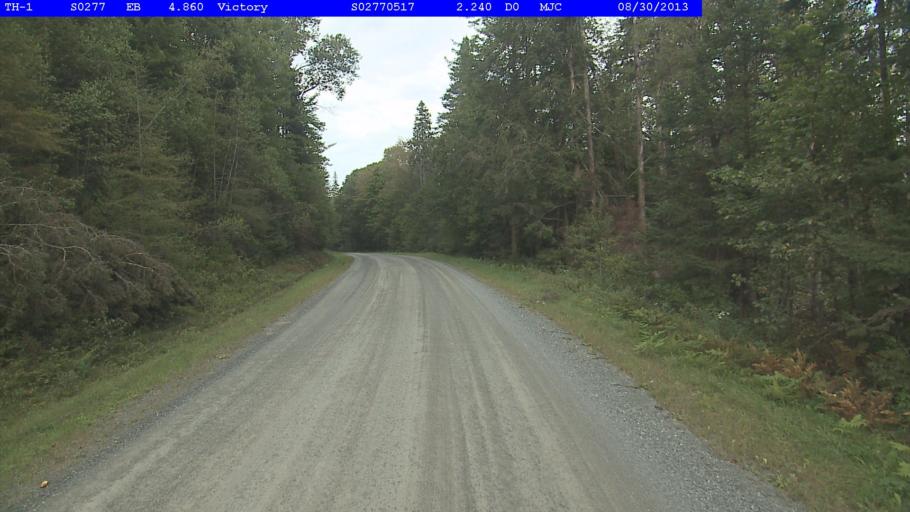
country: US
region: Vermont
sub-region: Caledonia County
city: Lyndonville
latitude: 44.5174
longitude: -71.8230
